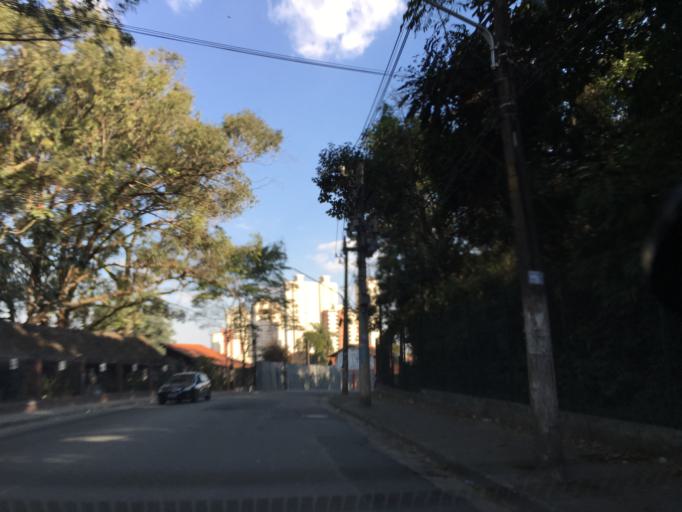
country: BR
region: Sao Paulo
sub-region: Sao Paulo
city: Sao Paulo
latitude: -23.4655
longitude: -46.6299
